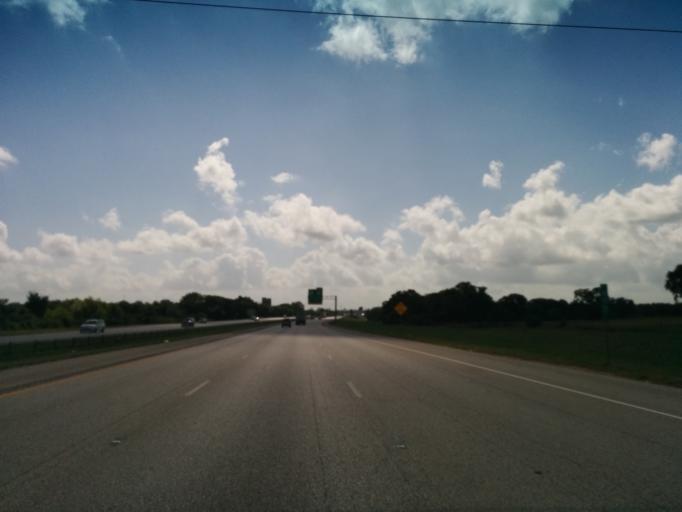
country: US
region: Texas
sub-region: Colorado County
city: Columbus
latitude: 29.6936
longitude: -96.5621
